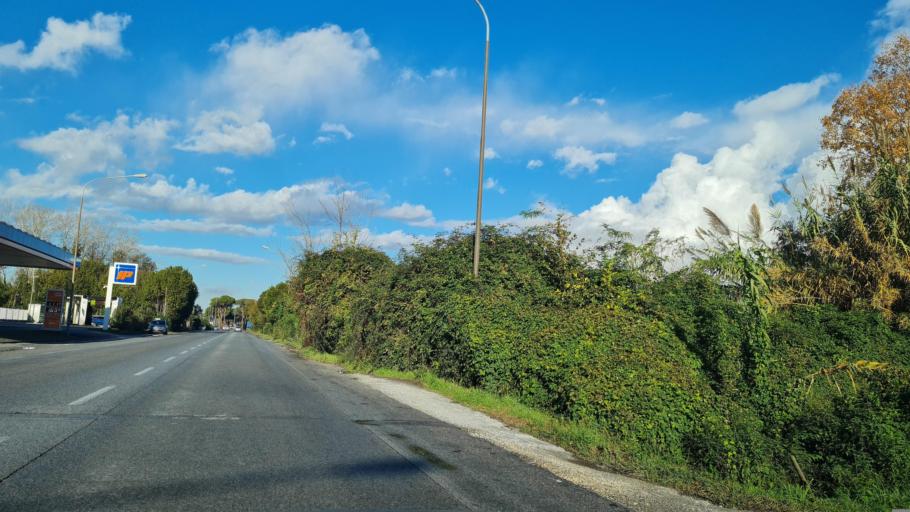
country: IT
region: Tuscany
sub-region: Provincia di Lucca
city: Pietrasanta
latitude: 43.9529
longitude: 10.2000
